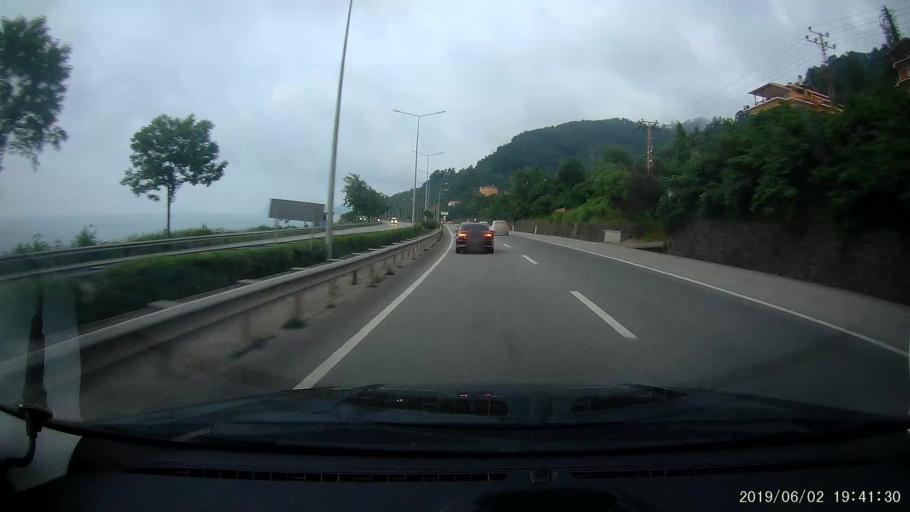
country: TR
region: Giresun
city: Kesap
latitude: 40.9134
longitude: 38.4814
